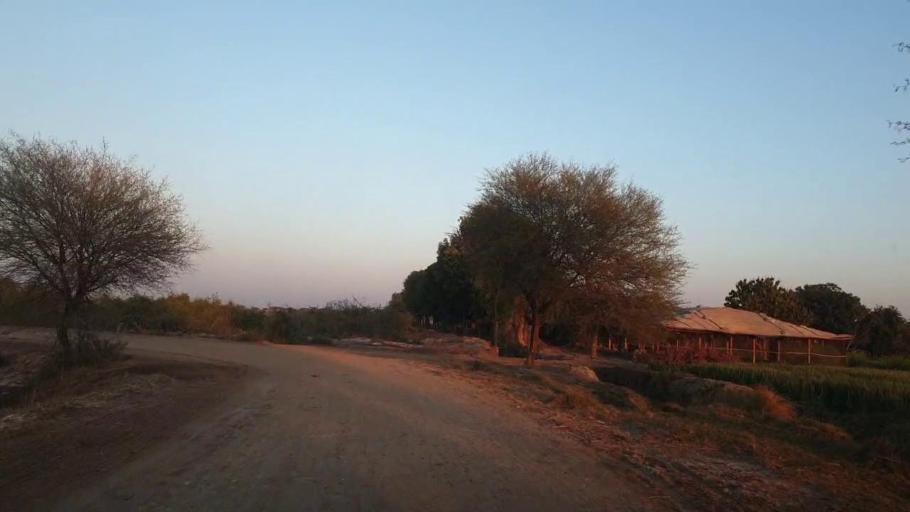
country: PK
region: Sindh
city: Mirpur Khas
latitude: 25.6951
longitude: 69.0530
